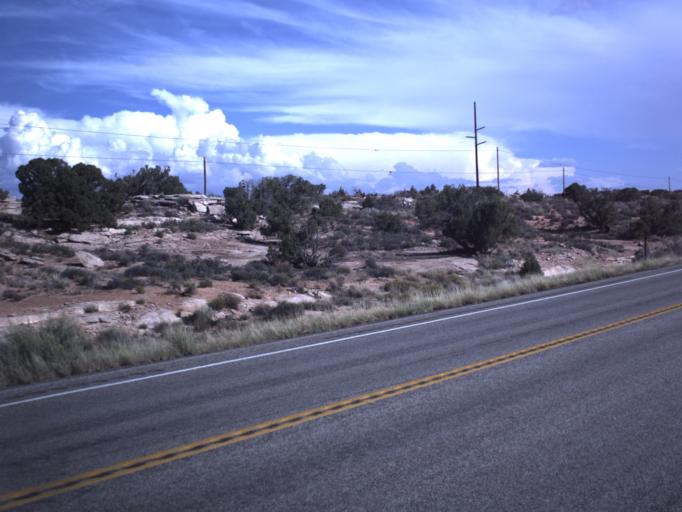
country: US
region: Utah
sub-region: Grand County
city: Moab
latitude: 38.6900
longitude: -109.6967
